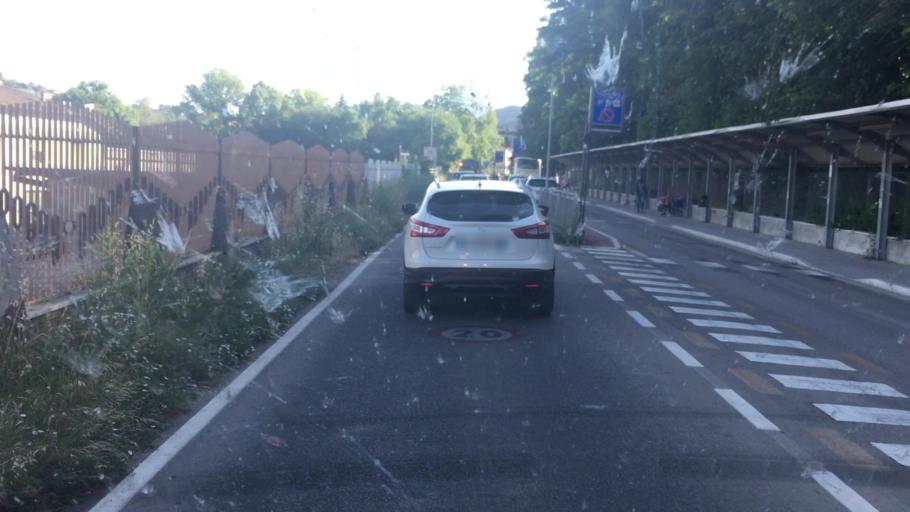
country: IT
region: Basilicate
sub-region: Provincia di Potenza
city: Potenza
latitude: 40.6296
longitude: 15.8080
